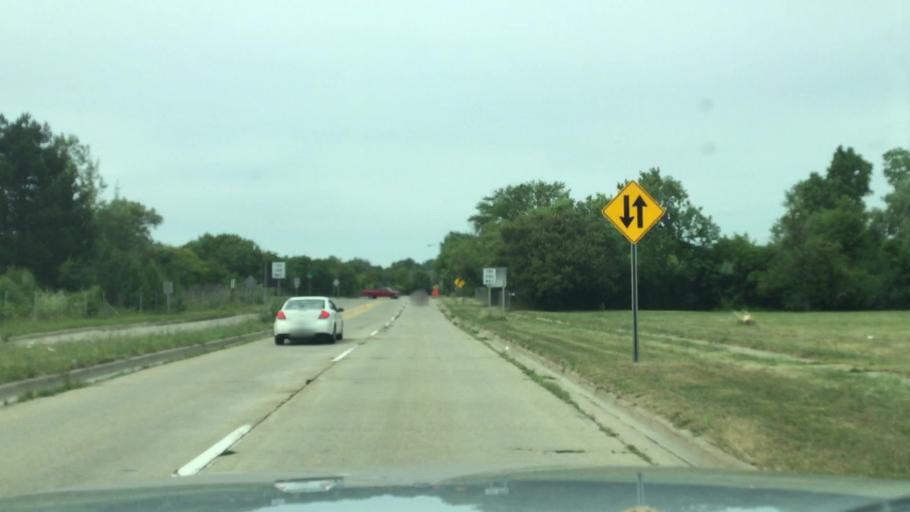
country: US
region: Michigan
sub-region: Genesee County
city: Beecher
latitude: 43.0824
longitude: -83.6847
